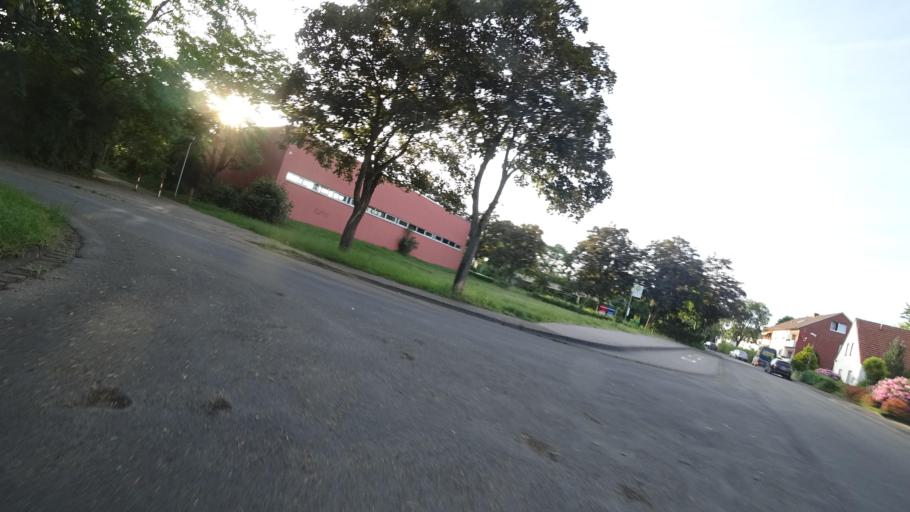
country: DE
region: North Rhine-Westphalia
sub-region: Regierungsbezirk Detmold
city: Guetersloh
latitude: 51.9014
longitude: 8.4115
